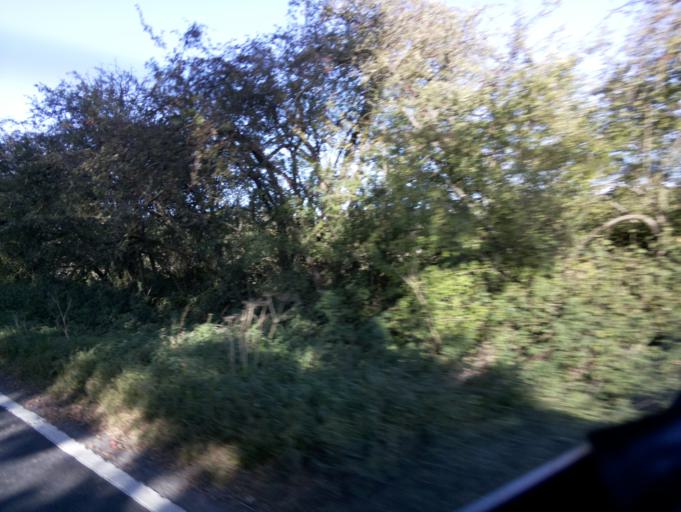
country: GB
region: England
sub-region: Hampshire
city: Swanmore
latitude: 50.9916
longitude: -1.1193
